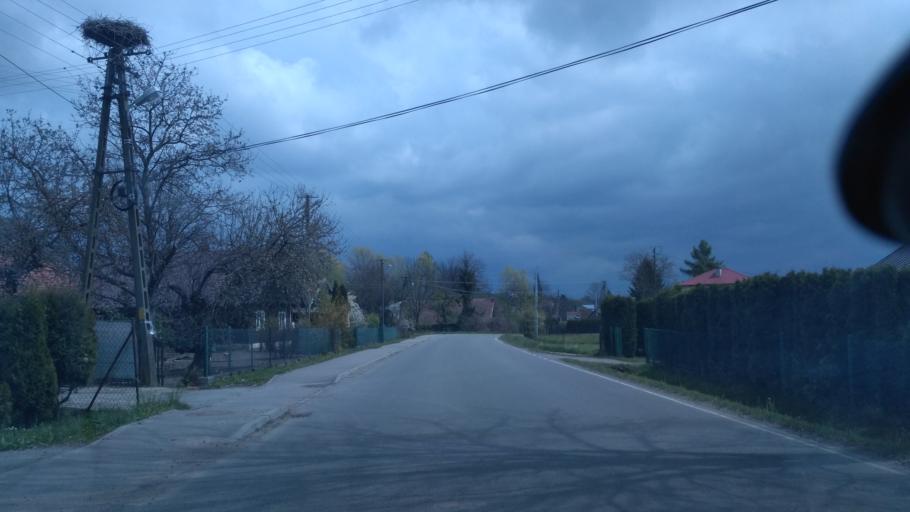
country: PL
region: Subcarpathian Voivodeship
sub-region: Powiat brzozowski
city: Haczow
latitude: 49.6456
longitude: 21.9288
